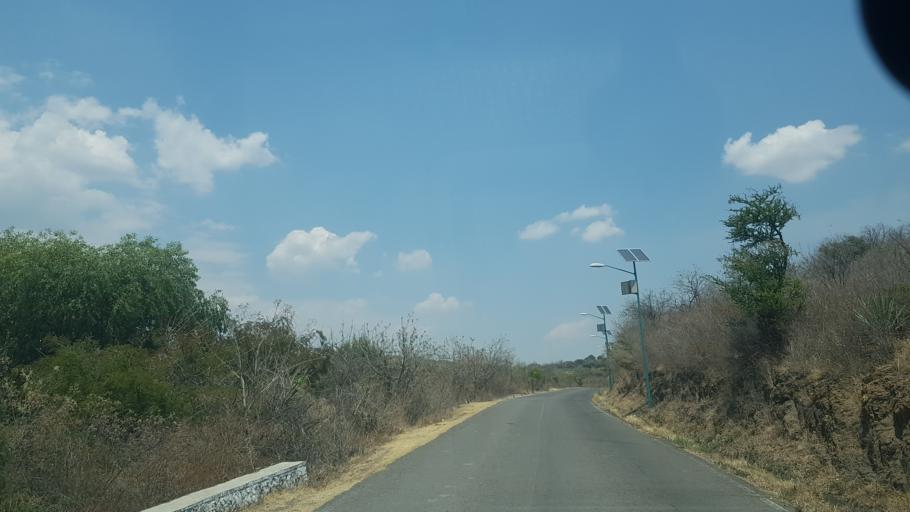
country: MX
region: Puebla
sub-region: Atzitzihuacan
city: Santiago Atzitzihuacan
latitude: 18.8339
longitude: -98.5797
